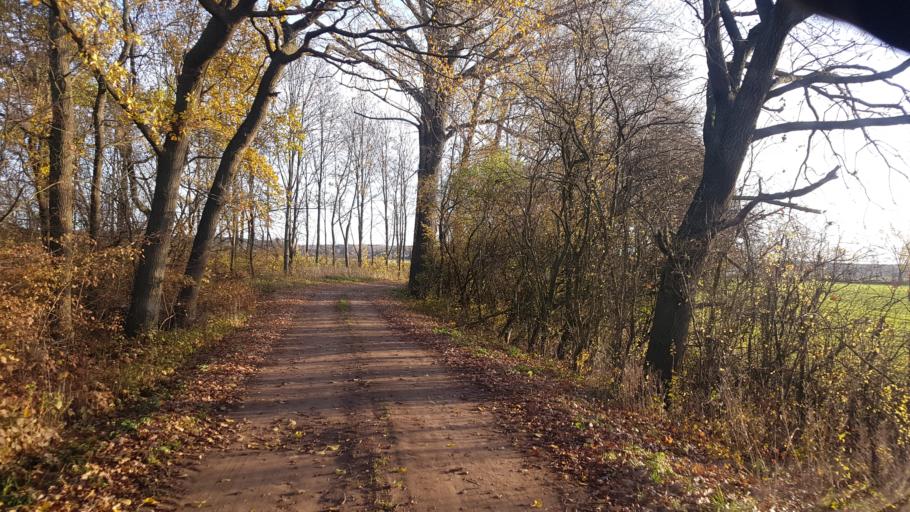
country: DE
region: Brandenburg
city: Sonnewalde
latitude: 51.7005
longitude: 13.7038
